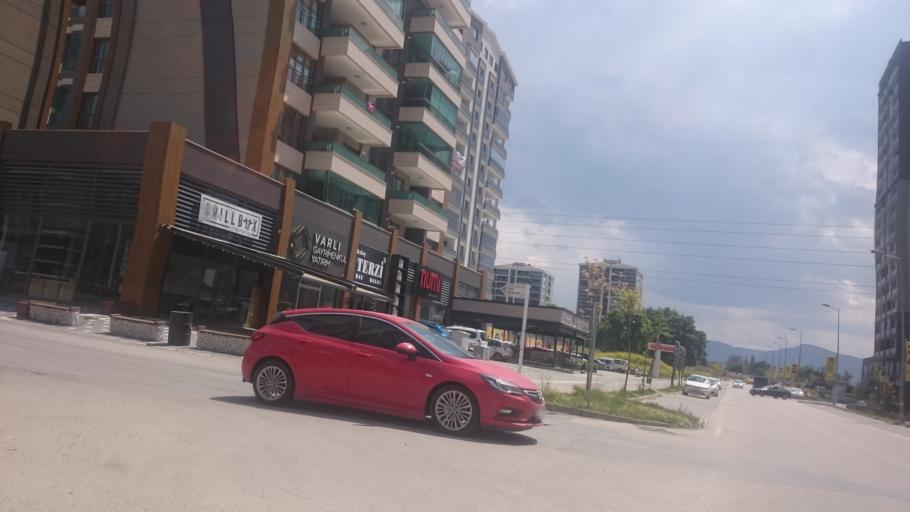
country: TR
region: Bursa
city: Cali
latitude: 40.2188
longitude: 28.9454
